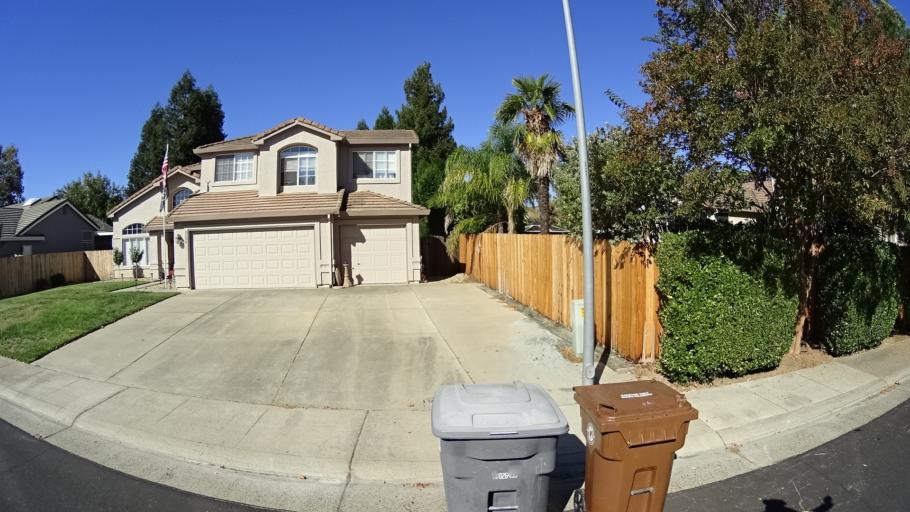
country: US
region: California
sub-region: Sacramento County
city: Elk Grove
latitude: 38.4193
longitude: -121.3652
